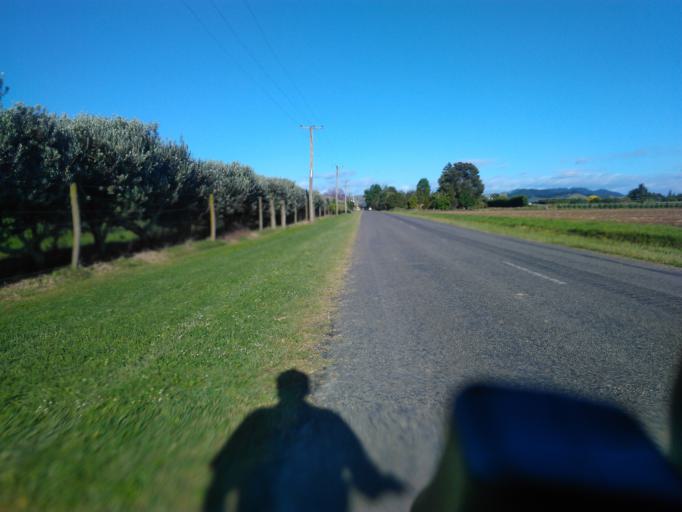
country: NZ
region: Gisborne
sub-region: Gisborne District
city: Gisborne
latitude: -38.5992
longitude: 177.9309
